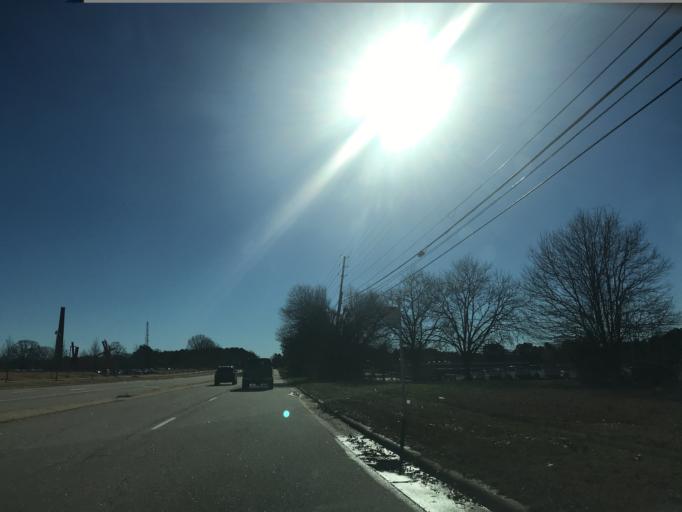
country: US
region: North Carolina
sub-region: Wake County
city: West Raleigh
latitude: 35.8095
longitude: -78.7057
